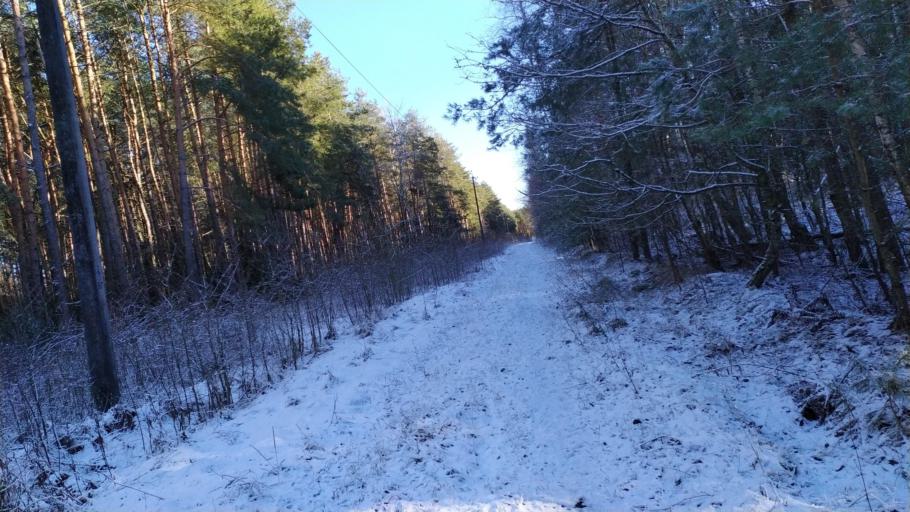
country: BY
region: Brest
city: Kamyanyets
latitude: 52.3799
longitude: 23.8642
